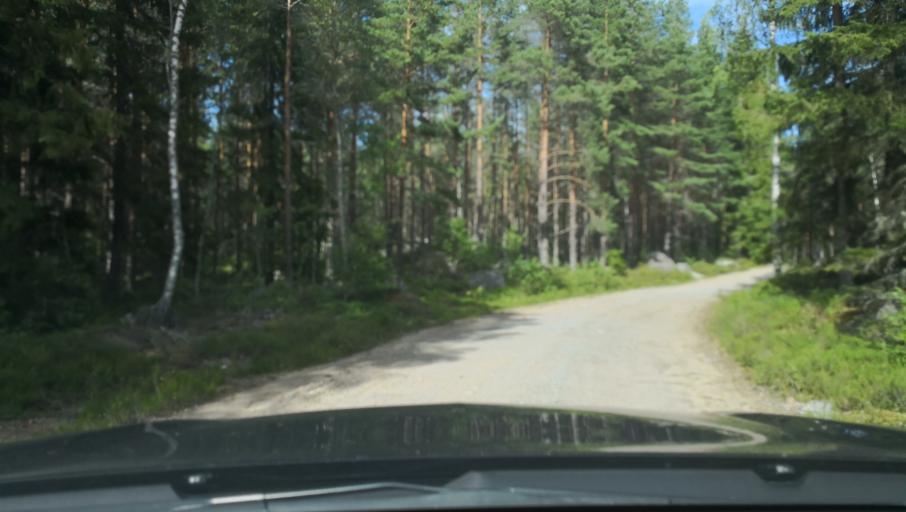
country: SE
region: Vaestmanland
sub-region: Surahammars Kommun
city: Surahammar
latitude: 59.6729
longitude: 16.1089
